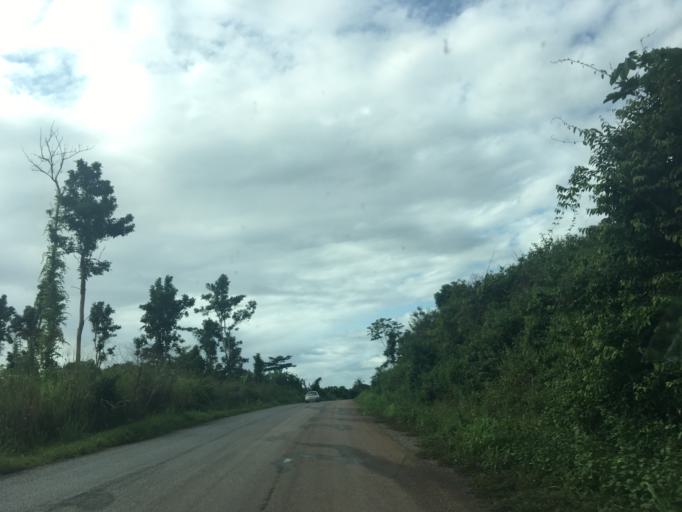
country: GH
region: Western
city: Wassa-Akropong
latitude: 6.0159
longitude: -2.4036
